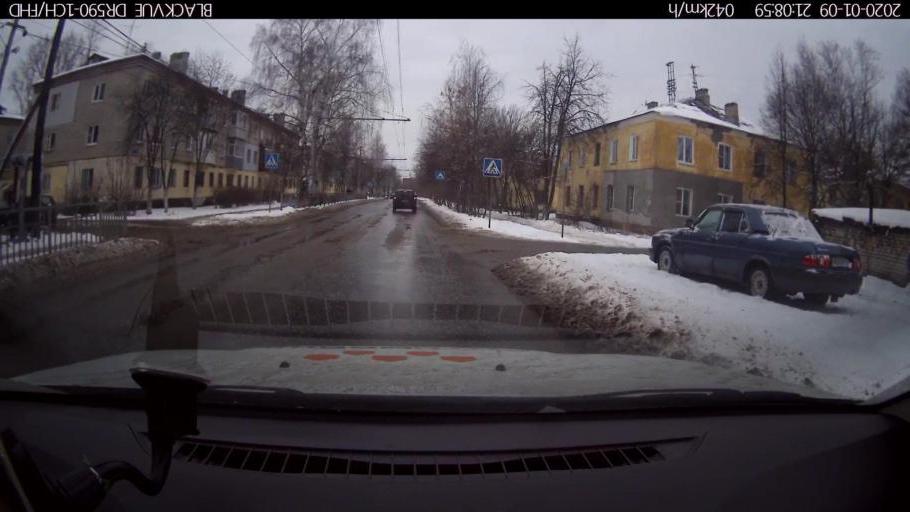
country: RU
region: Nizjnij Novgorod
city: Gorbatovka
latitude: 56.2922
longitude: 43.8603
